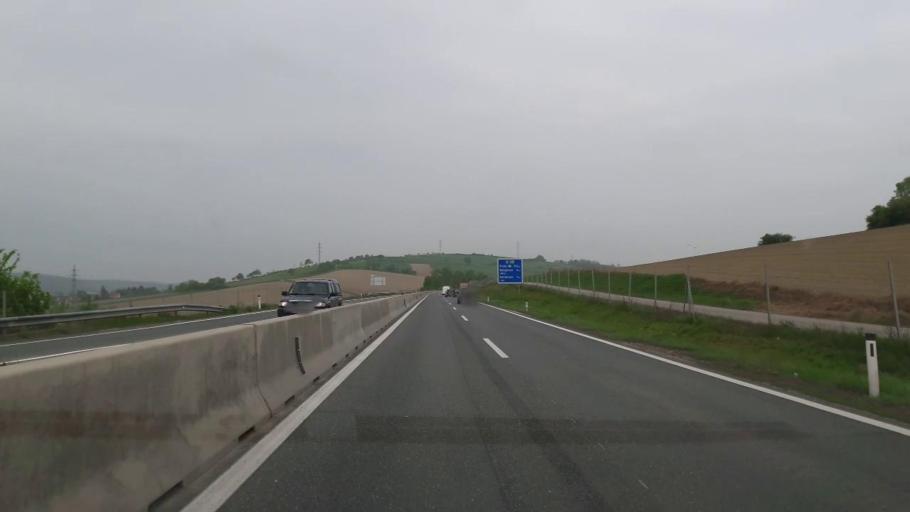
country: AT
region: Lower Austria
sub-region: Politischer Bezirk Hollabrunn
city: Gollersdorf
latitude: 48.5100
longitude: 16.0925
